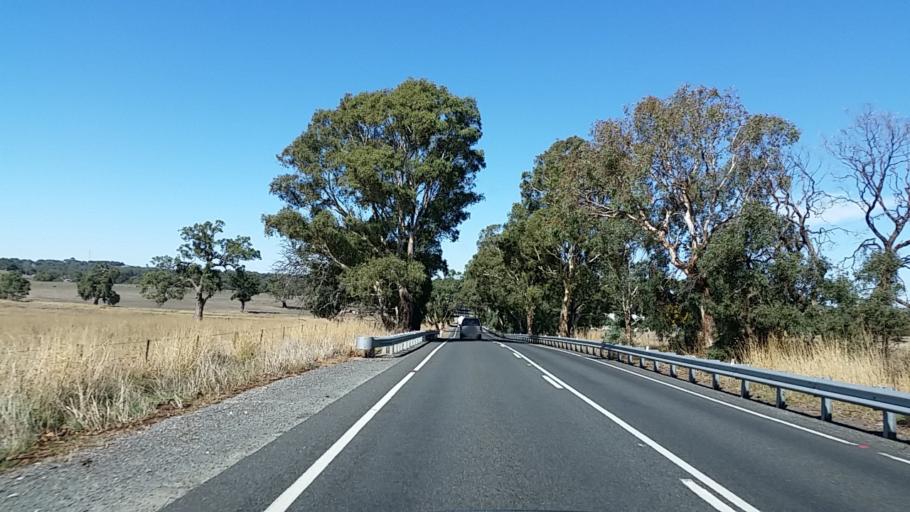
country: AU
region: South Australia
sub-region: Adelaide Hills
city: Birdwood
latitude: -34.7722
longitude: 139.0268
